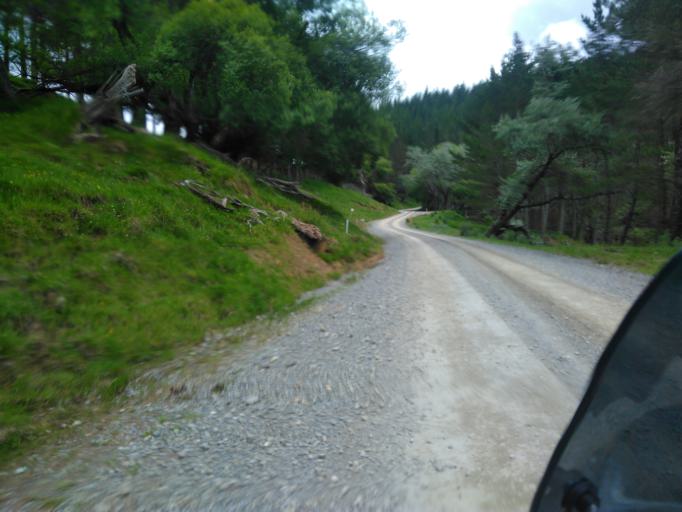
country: NZ
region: Gisborne
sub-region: Gisborne District
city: Gisborne
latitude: -38.0973
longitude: 178.1075
